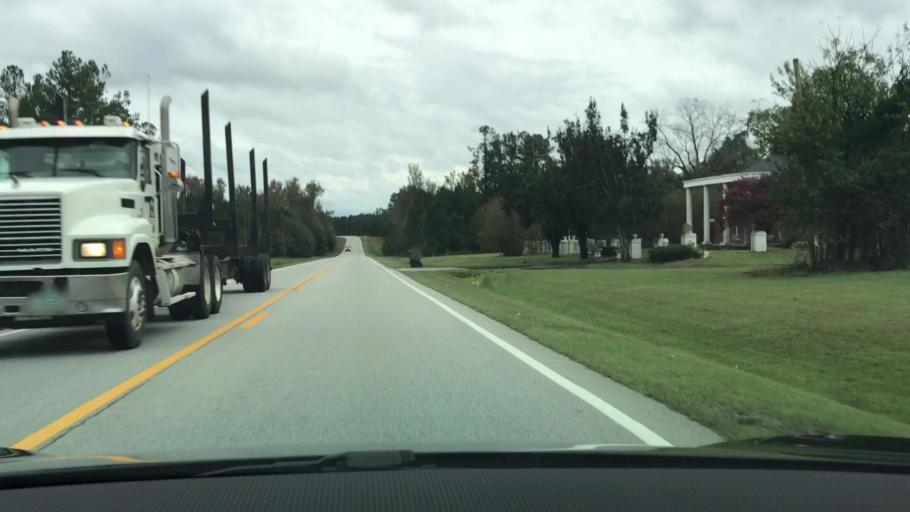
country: US
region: Georgia
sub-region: Glascock County
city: Gibson
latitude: 33.2704
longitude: -82.4961
